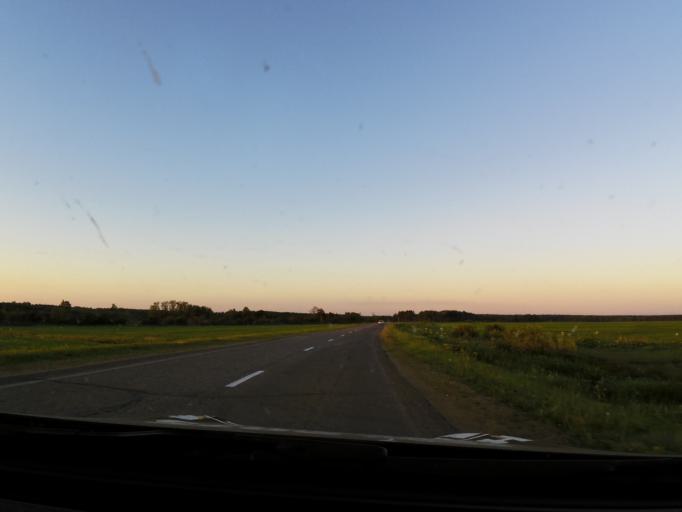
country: RU
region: Jaroslavl
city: Lyubim
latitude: 58.3687
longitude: 40.7234
